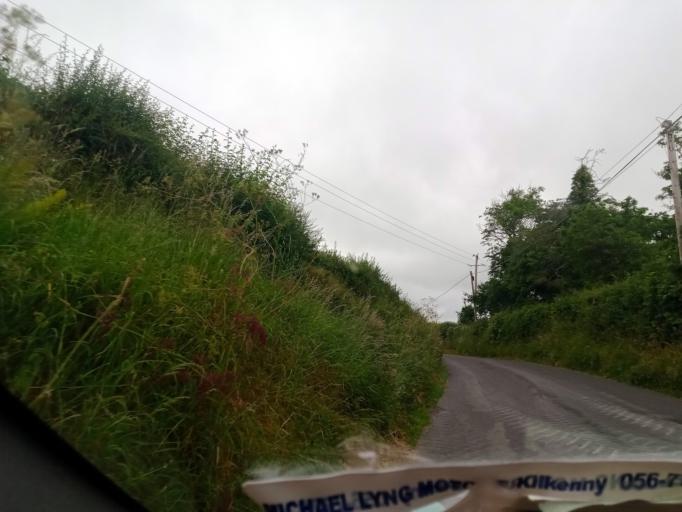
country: IE
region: Leinster
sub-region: Kilkenny
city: Ballyragget
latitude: 52.7509
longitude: -7.4338
